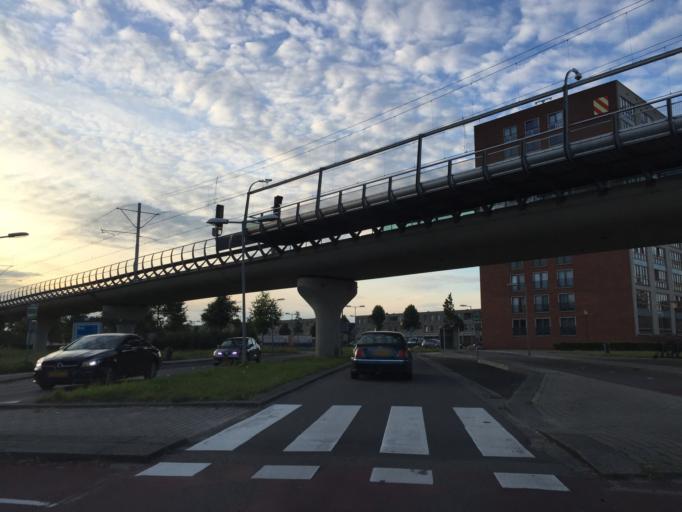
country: NL
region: South Holland
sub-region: Gemeente Rijnwoude
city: Benthuizen
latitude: 52.0651
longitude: 4.5342
